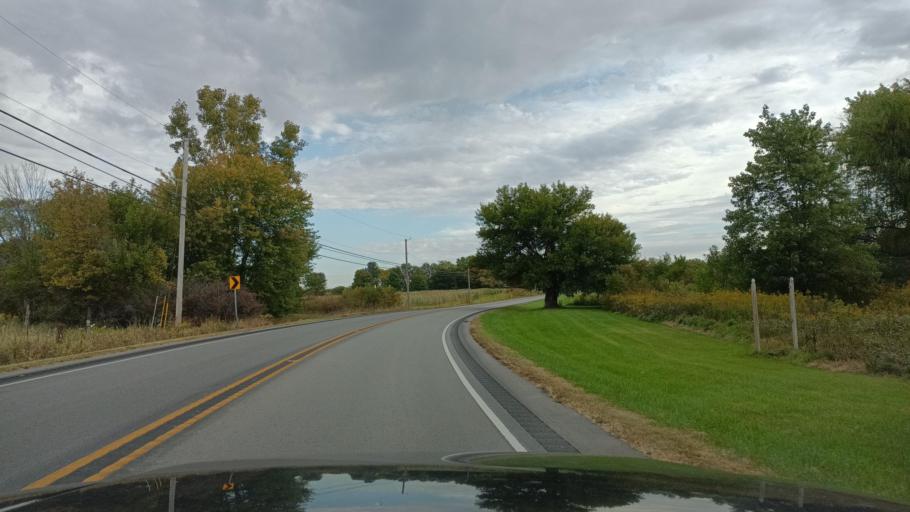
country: US
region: Indiana
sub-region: Delaware County
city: Daleville
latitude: 40.1459
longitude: -85.5421
